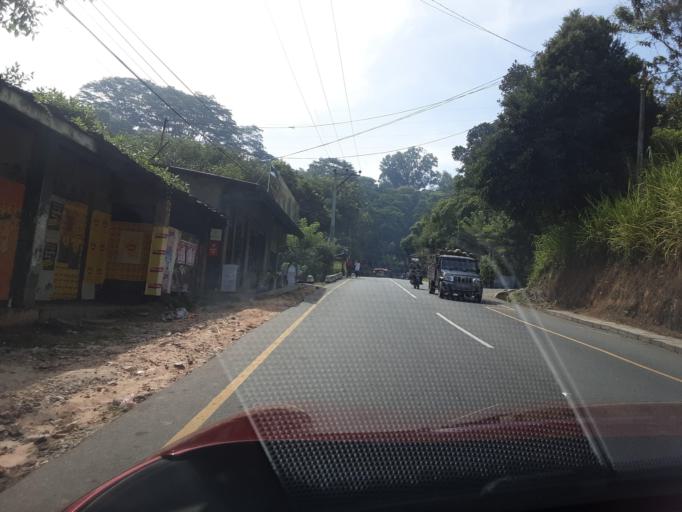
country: LK
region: Uva
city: Badulla
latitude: 6.9845
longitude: 81.0745
